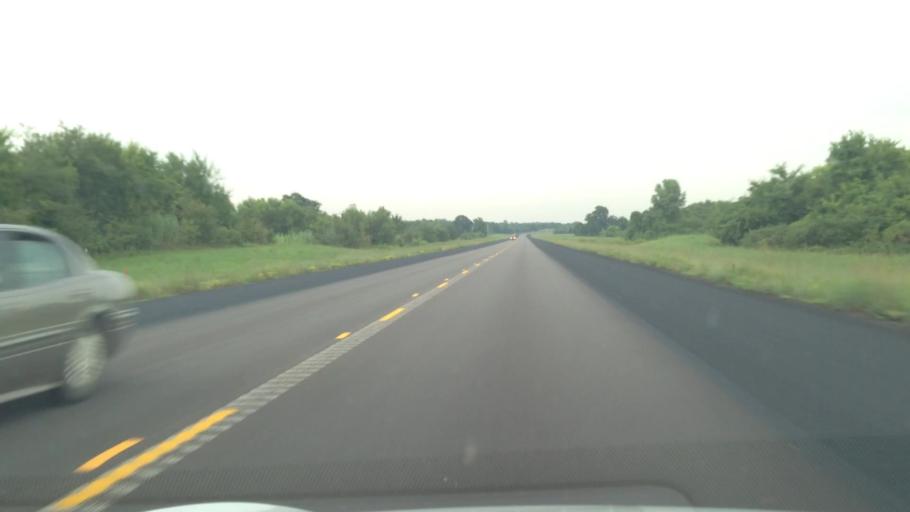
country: US
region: Kansas
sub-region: Cherokee County
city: Baxter Springs
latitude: 37.0366
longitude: -94.7077
